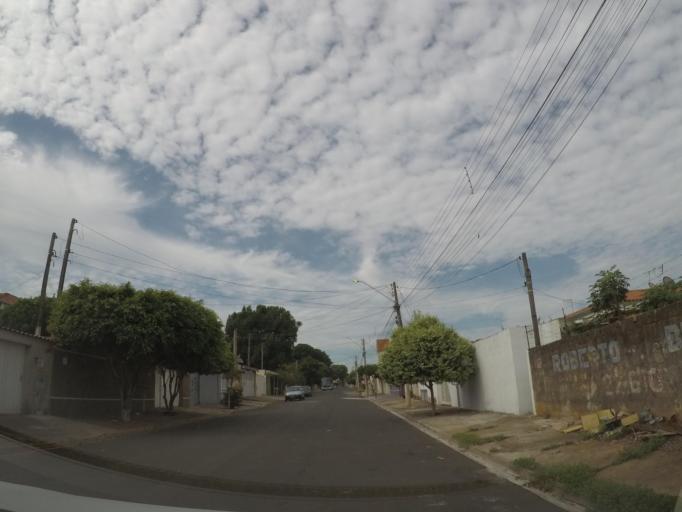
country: BR
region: Sao Paulo
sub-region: Hortolandia
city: Hortolandia
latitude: -22.8280
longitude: -47.1878
